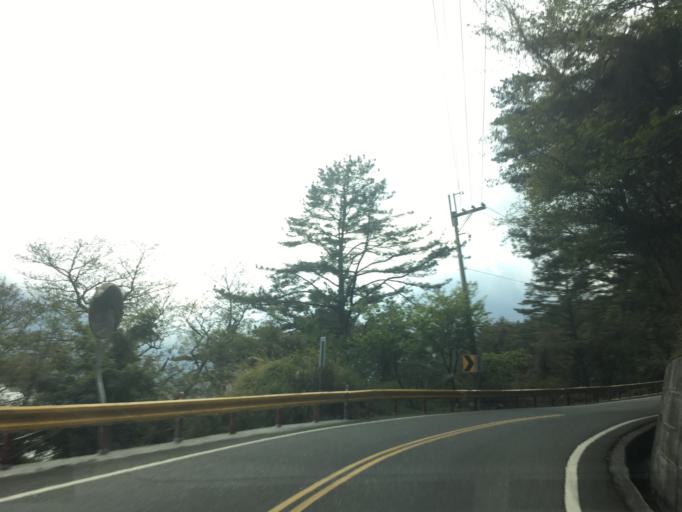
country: TW
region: Taiwan
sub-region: Hualien
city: Hualian
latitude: 24.1885
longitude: 121.3338
